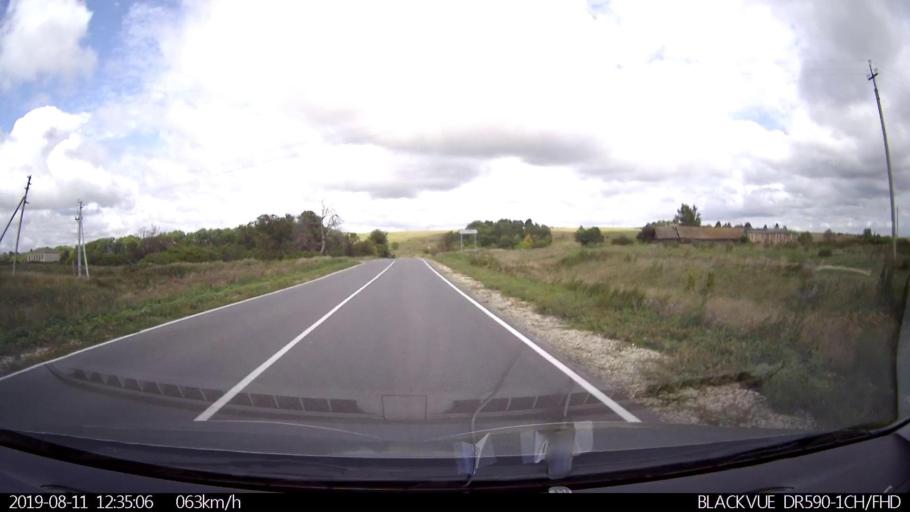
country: RU
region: Ulyanovsk
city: Ignatovka
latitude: 53.8219
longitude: 47.8346
